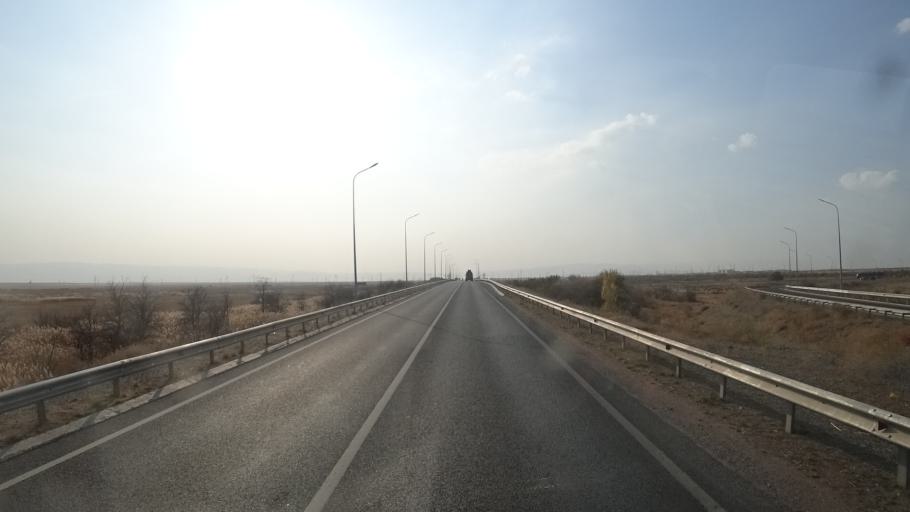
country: KZ
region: Zhambyl
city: Taraz
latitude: 42.8237
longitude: 71.1672
